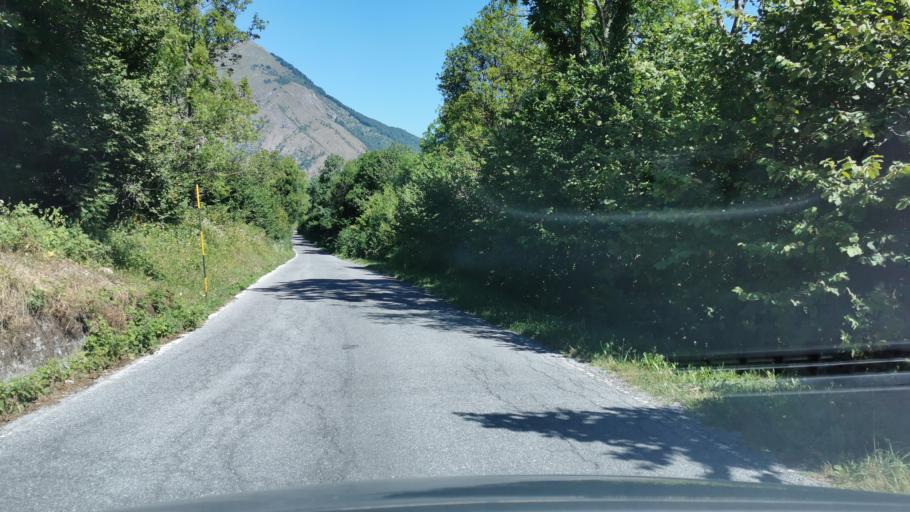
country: IT
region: Piedmont
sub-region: Provincia di Cuneo
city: Entracque
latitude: 44.2415
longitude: 7.3900
